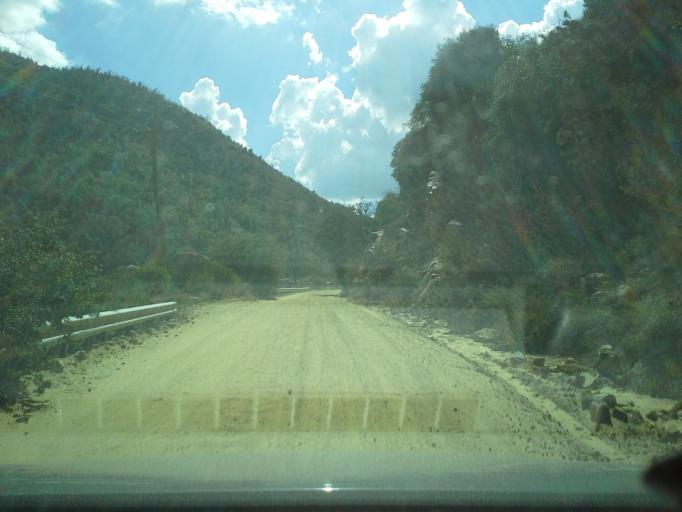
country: US
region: Arizona
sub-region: Yavapai County
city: Mayer
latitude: 34.2123
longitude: -112.3279
